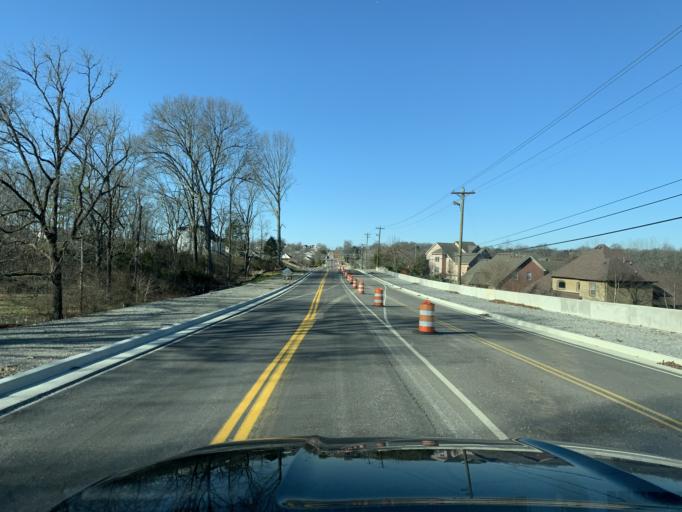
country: US
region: Tennessee
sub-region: Maury County
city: Spring Hill
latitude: 35.7527
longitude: -86.8891
